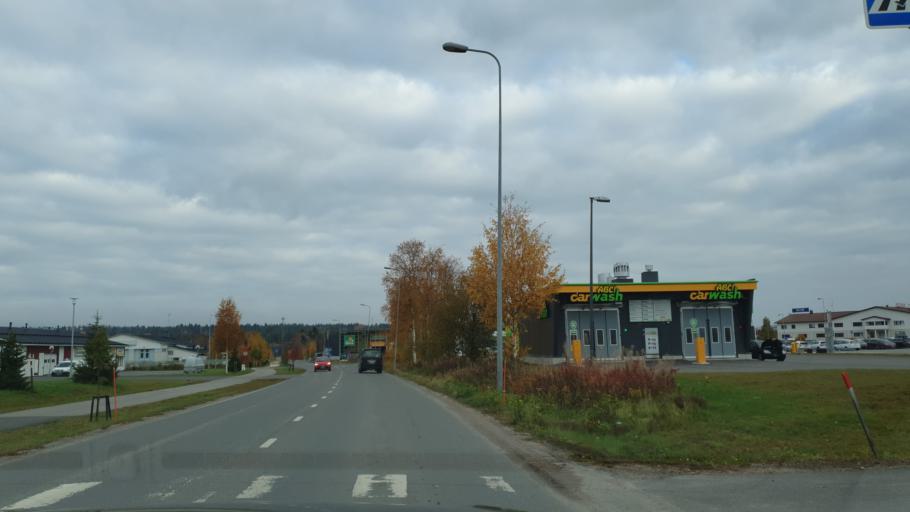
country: FI
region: Lapland
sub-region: Rovaniemi
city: Rovaniemi
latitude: 66.4927
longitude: 25.6836
